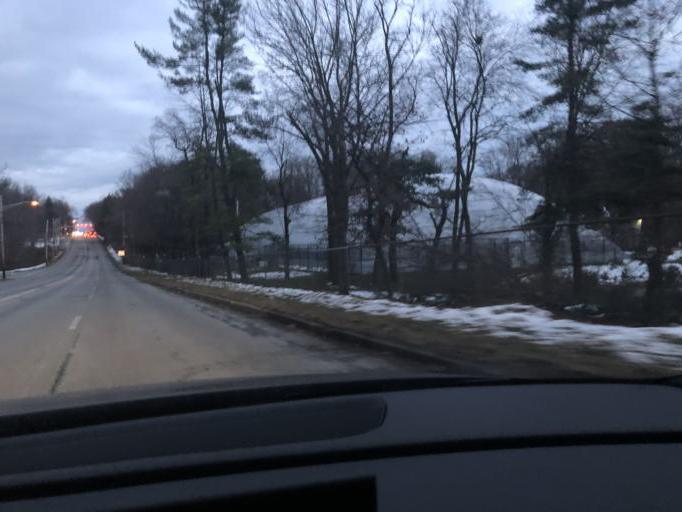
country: US
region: New Jersey
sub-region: Morris County
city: Morristown
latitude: 40.7954
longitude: -74.4528
